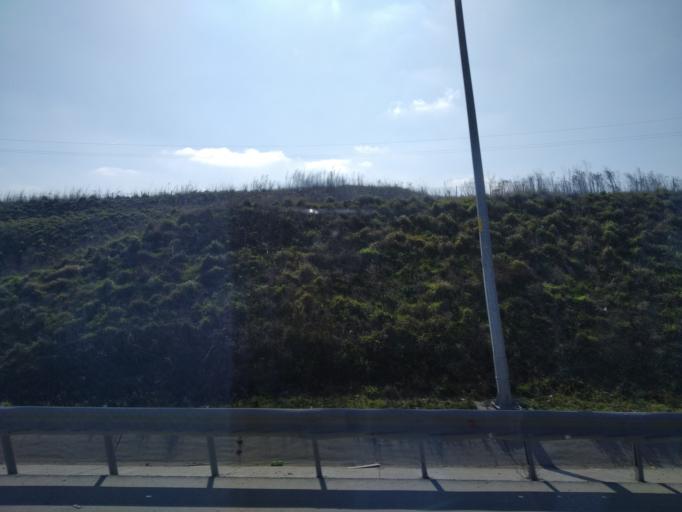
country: TR
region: Istanbul
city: Kemerburgaz
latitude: 41.2301
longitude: 28.8517
